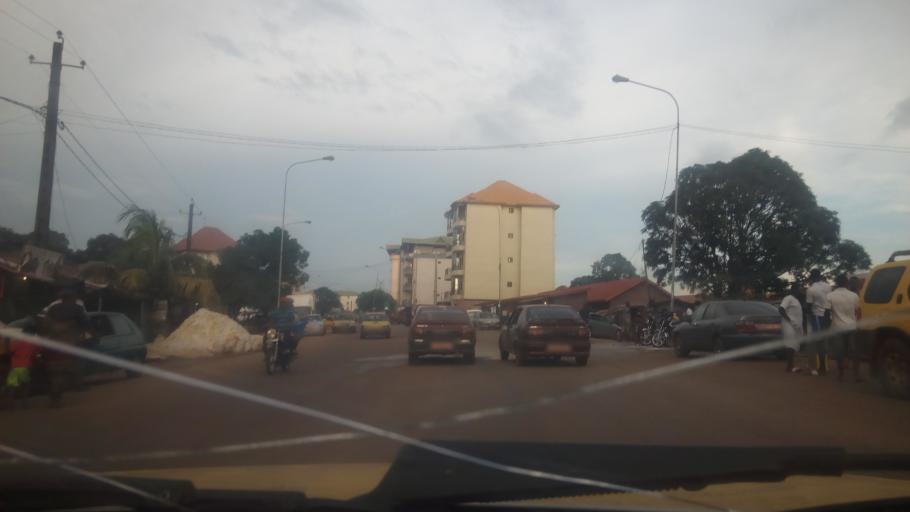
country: GN
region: Conakry
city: Conakry
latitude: 9.5696
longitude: -13.6486
